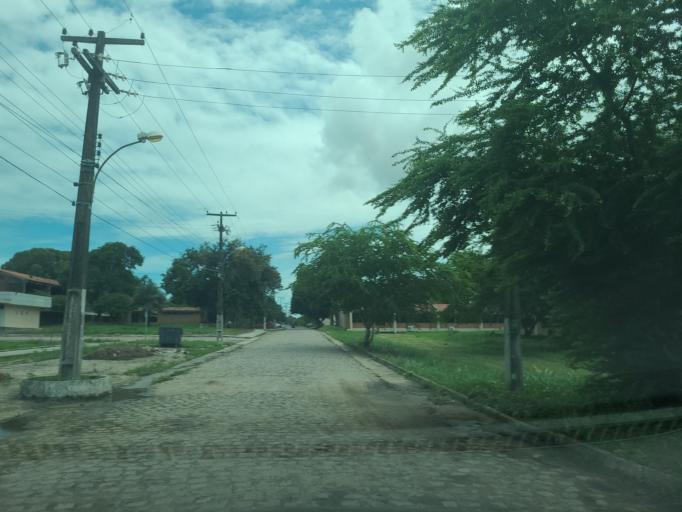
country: BR
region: Alagoas
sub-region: Satuba
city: Satuba
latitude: -9.5555
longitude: -35.7745
